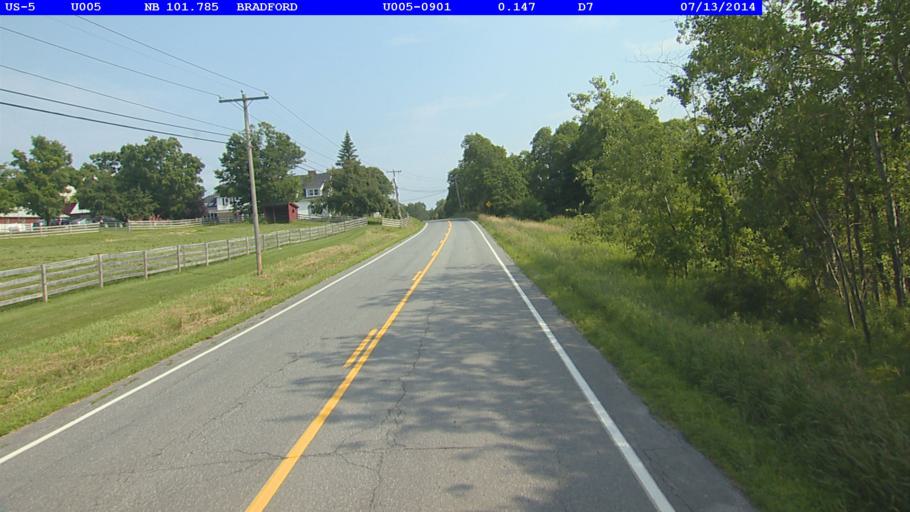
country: US
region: New Hampshire
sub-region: Grafton County
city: Orford
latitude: 43.9636
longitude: -72.1149
